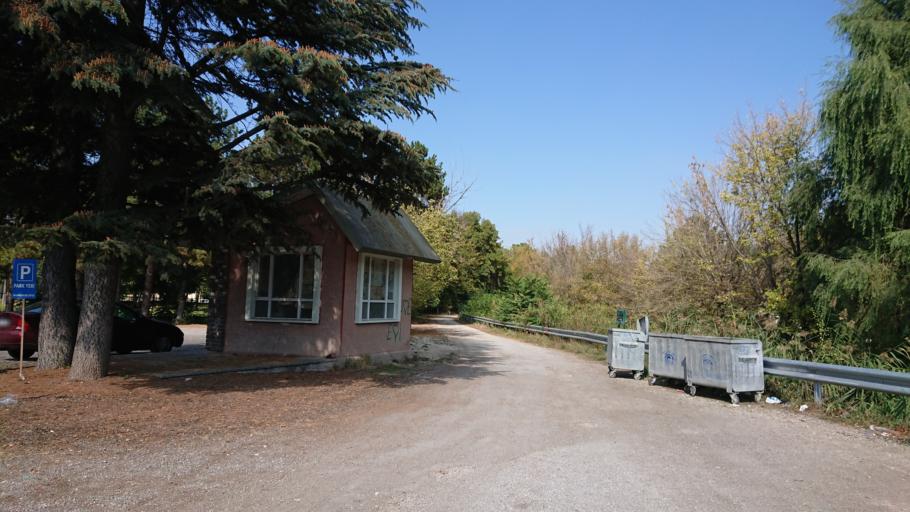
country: TR
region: Eskisehir
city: Eskisehir
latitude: 39.7444
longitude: 30.4656
